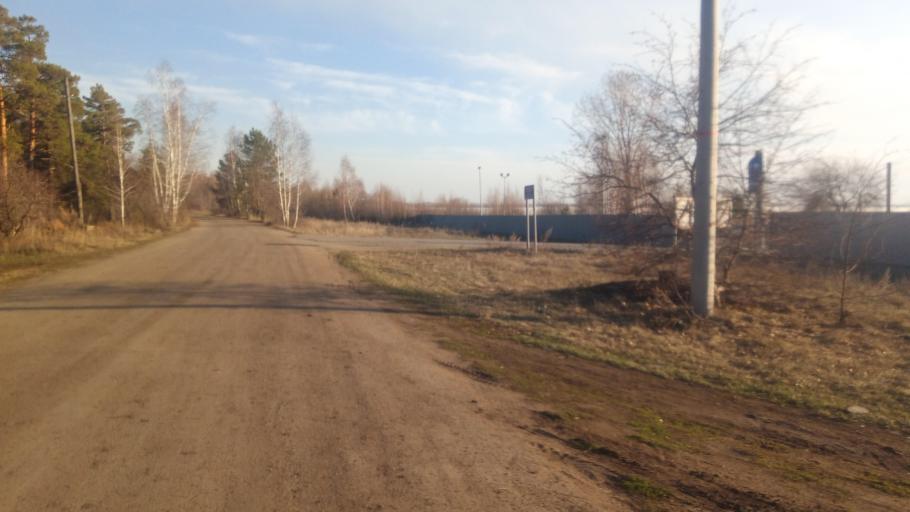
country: RU
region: Chelyabinsk
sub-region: Gorod Chelyabinsk
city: Chelyabinsk
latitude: 55.1365
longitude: 61.3274
